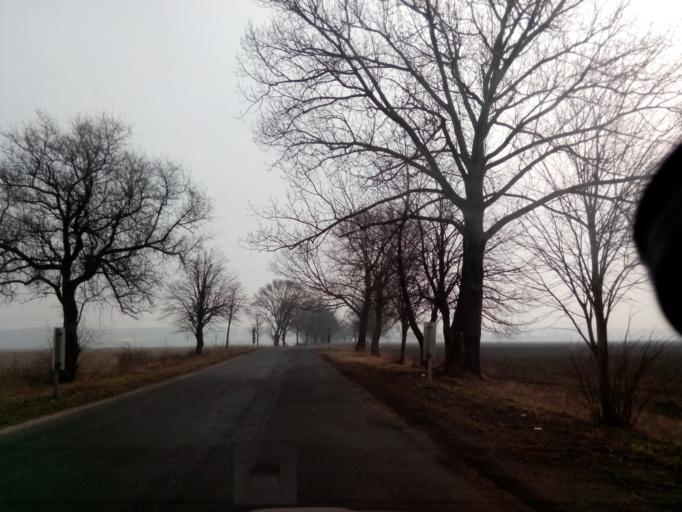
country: HU
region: Borsod-Abauj-Zemplen
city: Gonc
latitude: 48.4948
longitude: 21.2411
